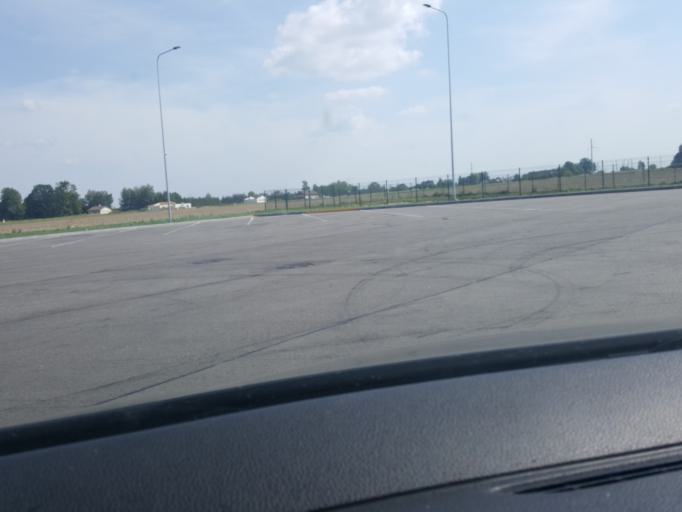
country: LT
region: Marijampoles apskritis
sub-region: Marijampole Municipality
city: Marijampole
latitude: 54.5582
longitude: 23.2751
